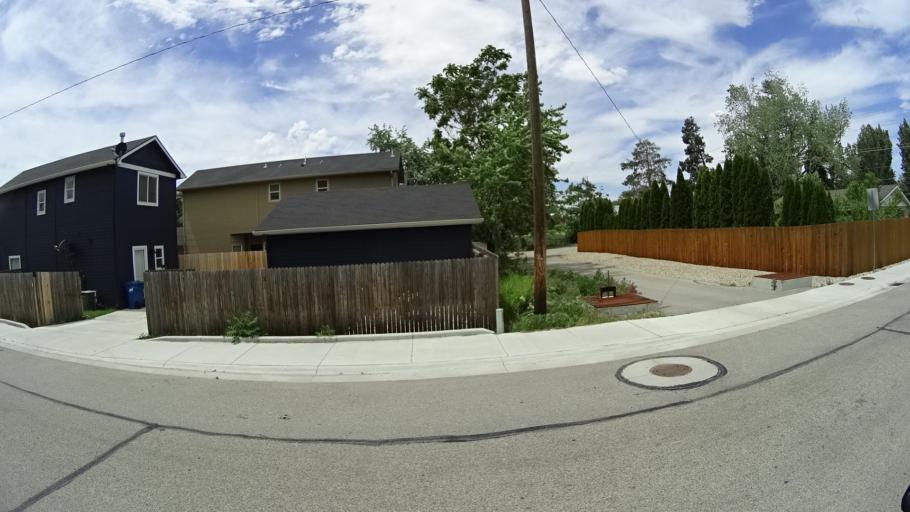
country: US
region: Idaho
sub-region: Ada County
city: Eagle
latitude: 43.6332
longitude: -116.3219
